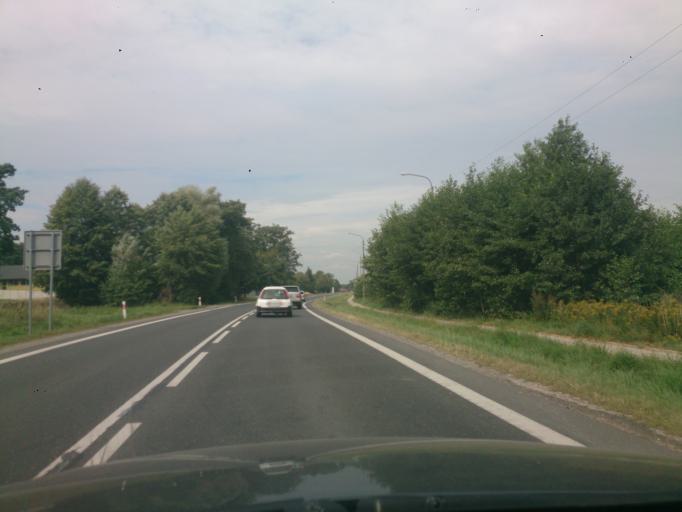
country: PL
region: Subcarpathian Voivodeship
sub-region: Powiat kolbuszowski
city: Kolbuszowa
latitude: 50.2113
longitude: 21.8219
